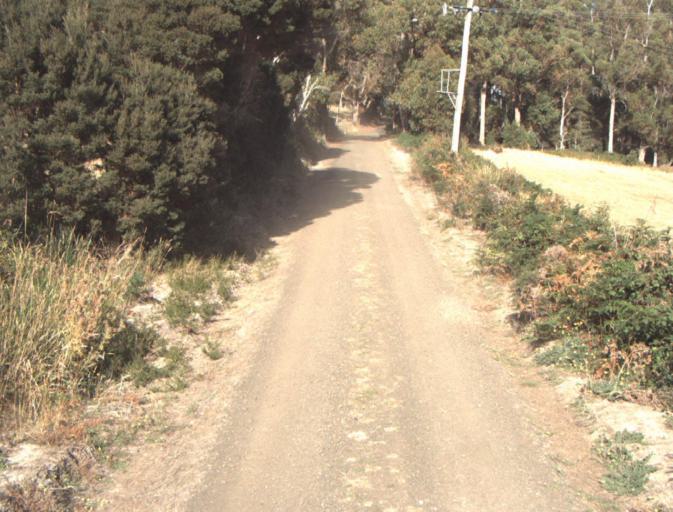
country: AU
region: Tasmania
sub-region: Dorset
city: Bridport
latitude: -41.1537
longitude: 147.2239
